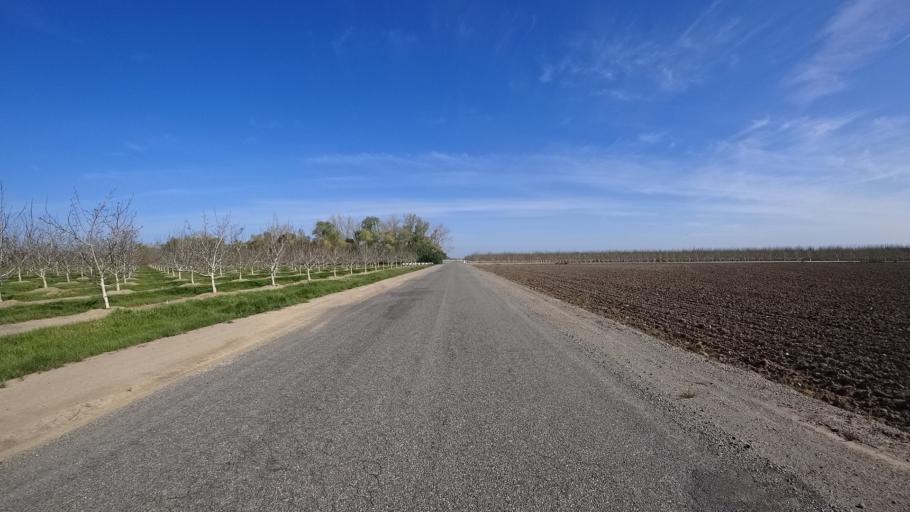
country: US
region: California
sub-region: Glenn County
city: Willows
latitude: 39.6183
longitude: -122.1170
